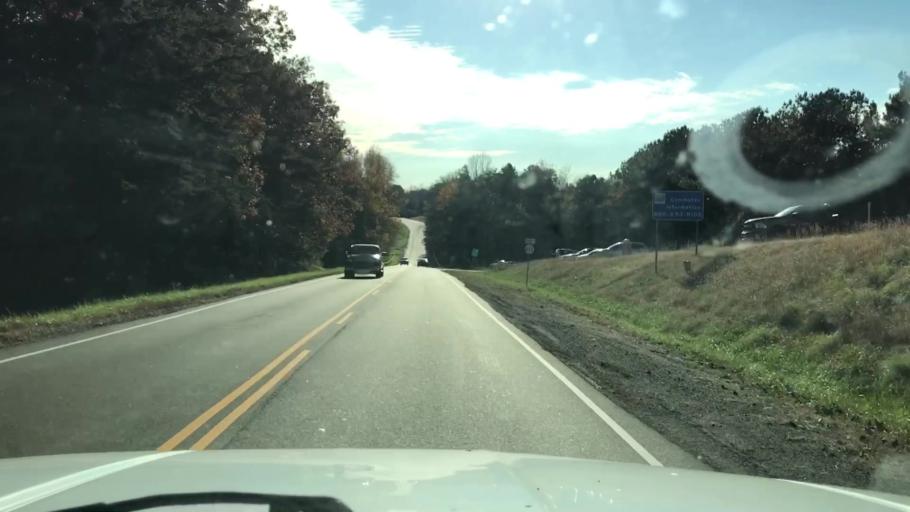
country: US
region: Virginia
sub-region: Goochland County
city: Goochland
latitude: 37.7093
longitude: -77.7836
